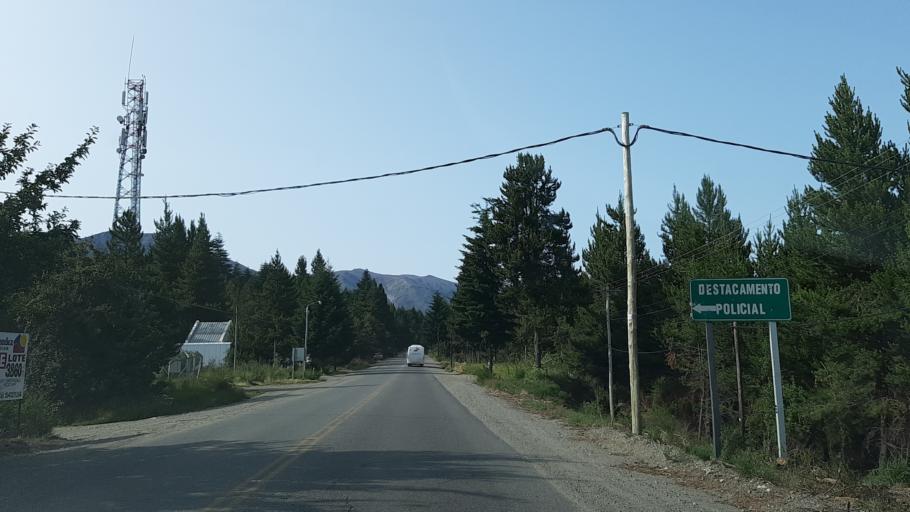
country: AR
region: Rio Negro
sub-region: Departamento de Bariloche
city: San Carlos de Bariloche
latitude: -41.1529
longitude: -71.4086
